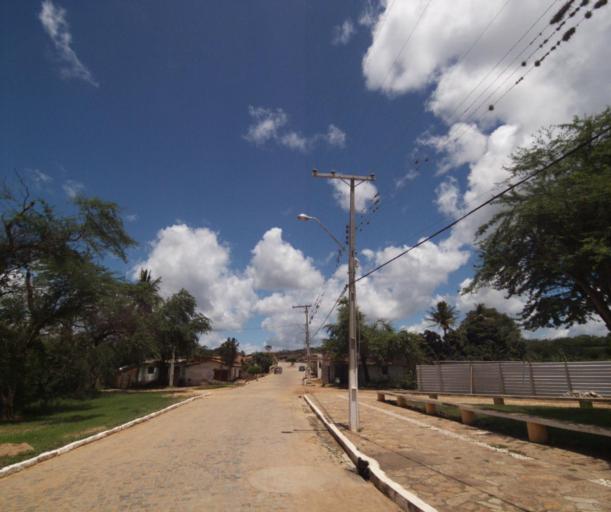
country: BR
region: Bahia
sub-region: Pocoes
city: Pocoes
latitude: -14.3752
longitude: -40.5031
